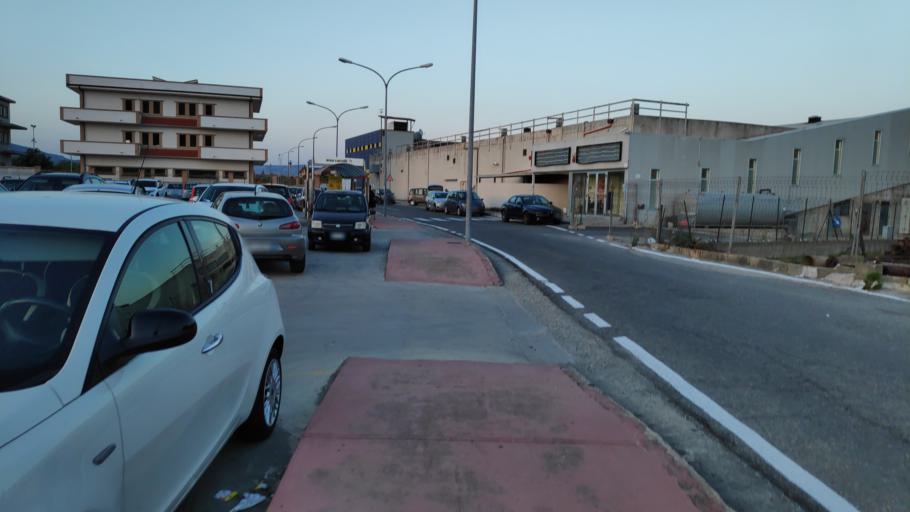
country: IT
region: Calabria
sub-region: Provincia di Reggio Calabria
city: Marina di Gioiosa Ionica
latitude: 38.2884
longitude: 16.3134
